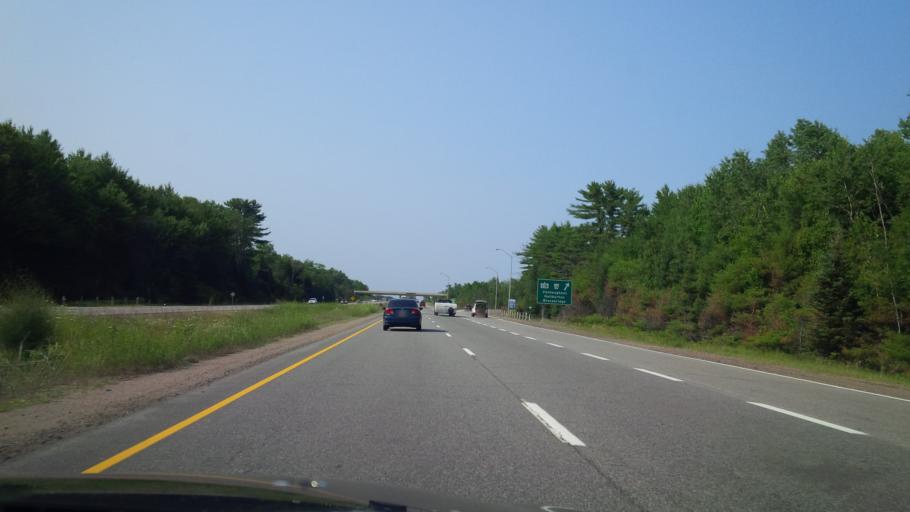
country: CA
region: Ontario
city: Bracebridge
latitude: 45.0007
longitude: -79.3033
